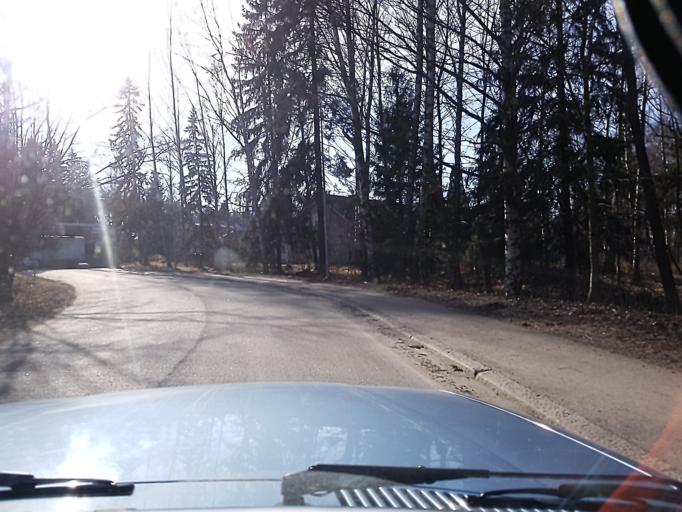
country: FI
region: Uusimaa
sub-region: Helsinki
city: Teekkarikylae
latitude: 60.1641
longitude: 24.8659
